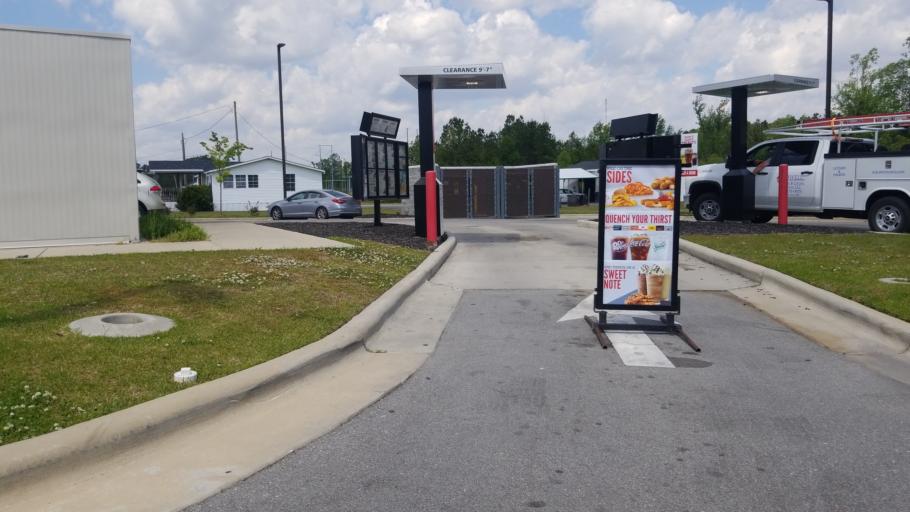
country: US
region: North Carolina
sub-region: Onslow County
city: Jacksonville
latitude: 34.7525
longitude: -77.4472
